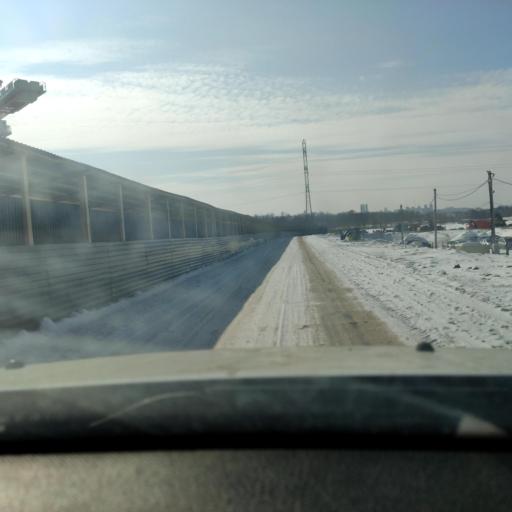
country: RU
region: Bashkortostan
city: Ufa
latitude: 54.7799
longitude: 55.9607
